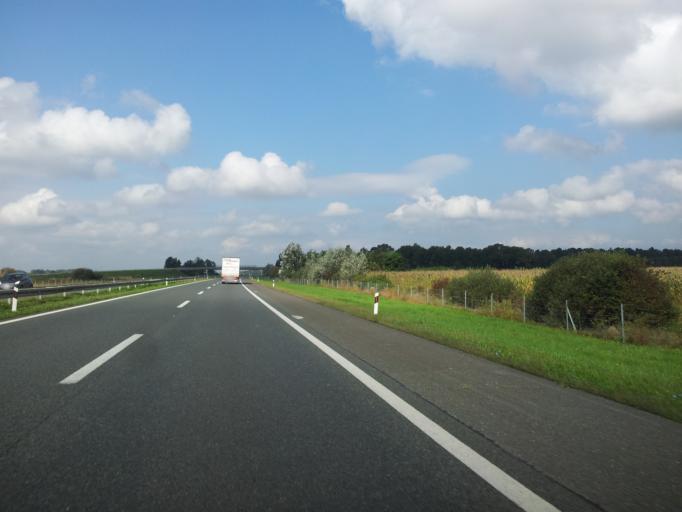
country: HR
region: Brodsko-Posavska
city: Resetari
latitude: 45.2198
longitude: 17.4997
